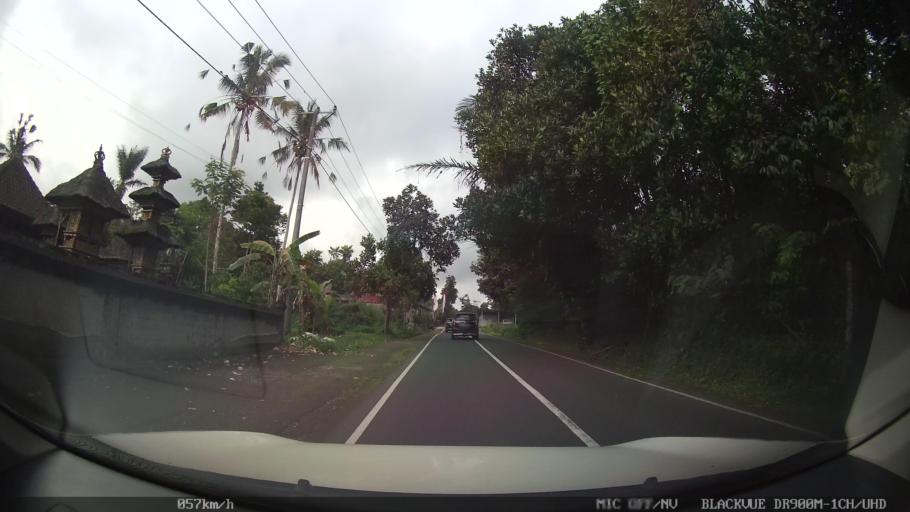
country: ID
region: Bali
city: Banjar Bias
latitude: -8.3777
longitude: 115.4182
